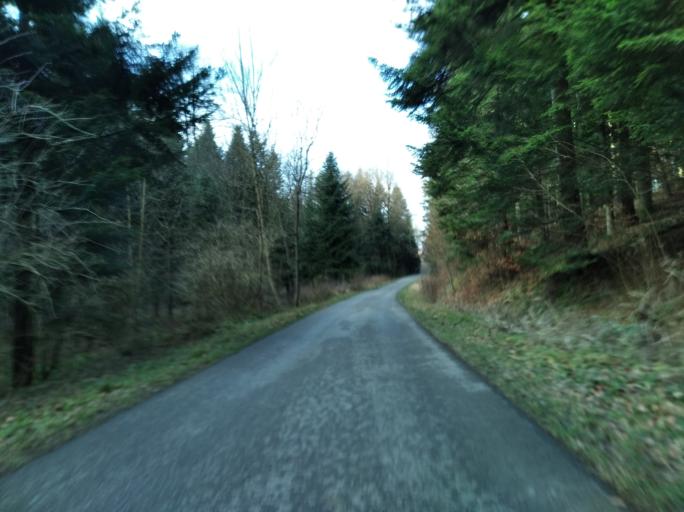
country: PL
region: Subcarpathian Voivodeship
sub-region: Powiat strzyzowski
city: Konieczkowa
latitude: 49.8262
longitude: 21.9429
